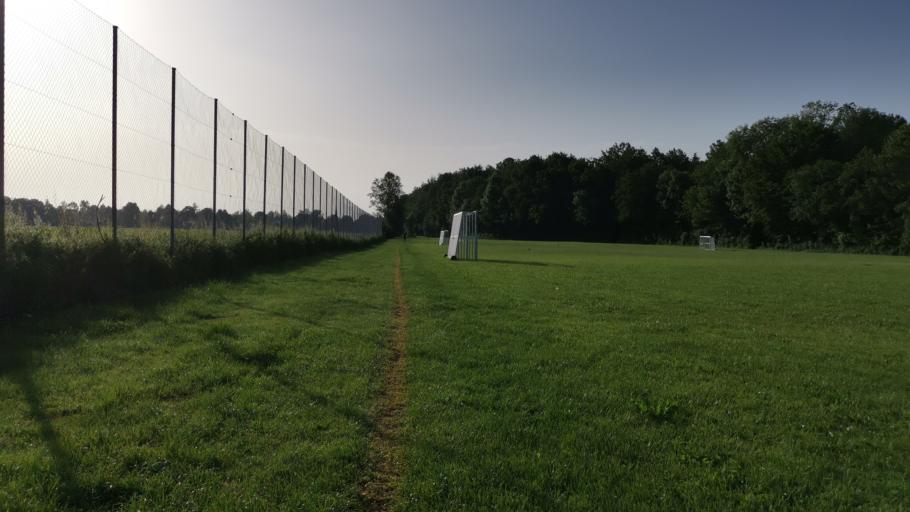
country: DE
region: Bavaria
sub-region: Upper Bavaria
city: Pullach im Isartal
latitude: 48.0625
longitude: 11.5069
